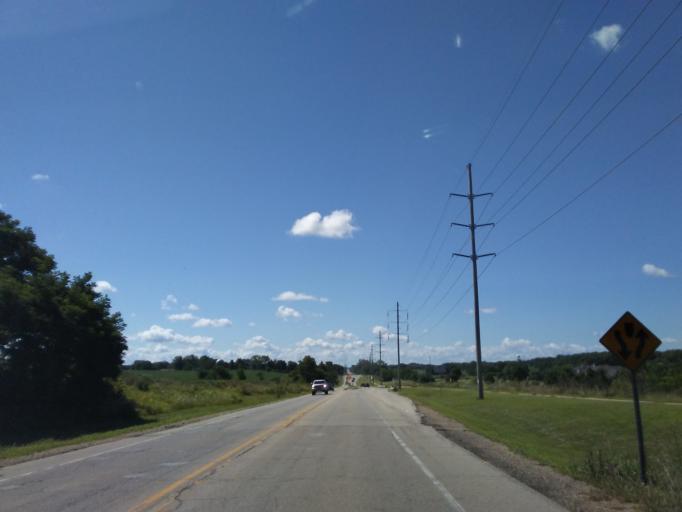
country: US
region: Wisconsin
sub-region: Dane County
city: Verona
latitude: 43.0383
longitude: -89.5330
